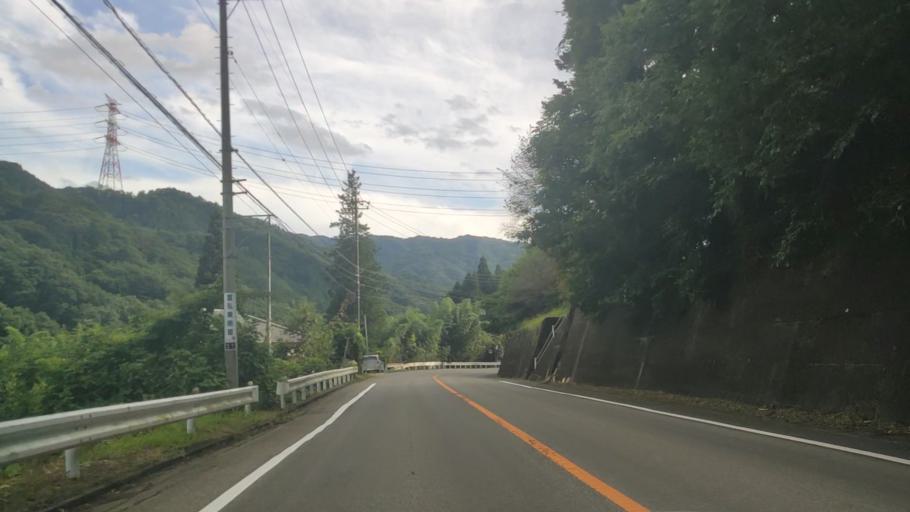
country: JP
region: Gunma
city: Kiryu
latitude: 36.5892
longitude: 139.4006
